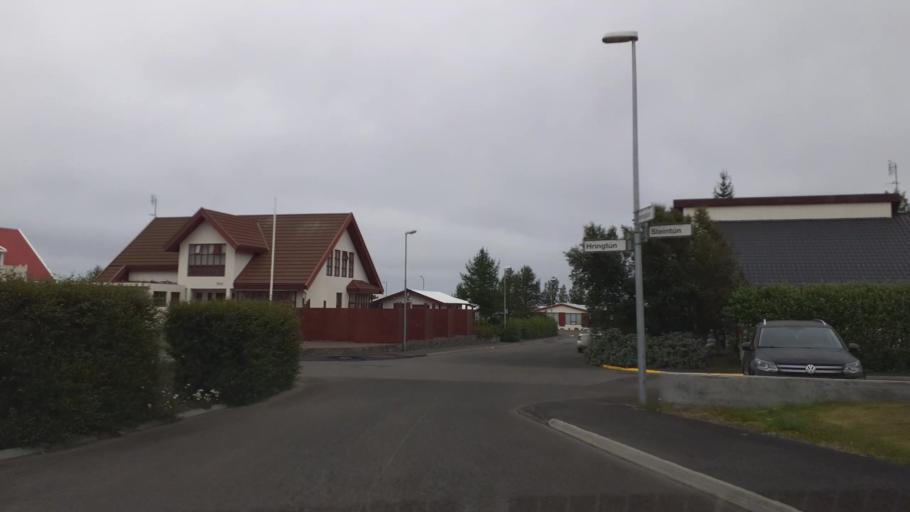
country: IS
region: Northeast
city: Dalvik
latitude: 65.9709
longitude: -18.5413
